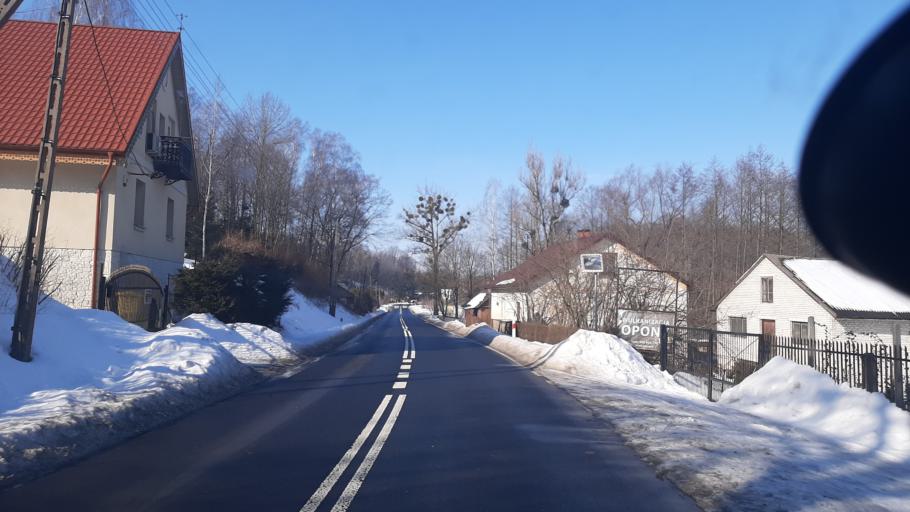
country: PL
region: Lublin Voivodeship
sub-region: Powiat pulawski
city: Wawolnica
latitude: 51.2899
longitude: 22.1602
